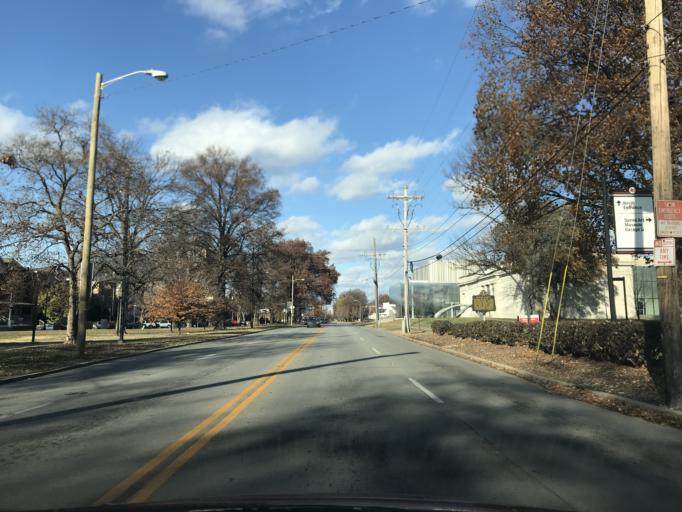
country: US
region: Kentucky
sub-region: Jefferson County
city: Louisville
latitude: 38.2166
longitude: -85.7619
